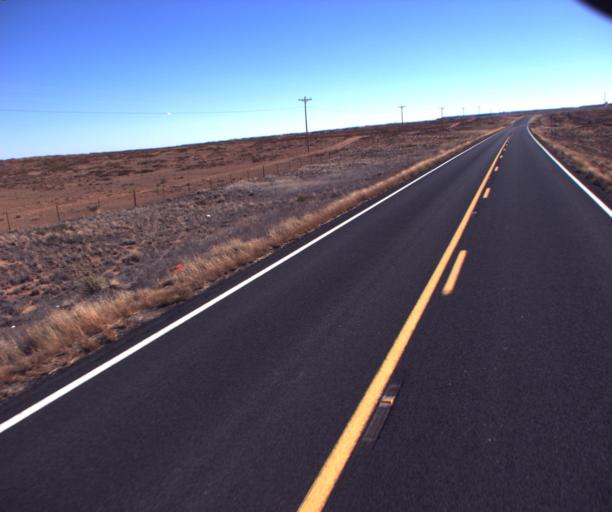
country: US
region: Arizona
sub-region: Coconino County
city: Tuba City
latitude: 36.0073
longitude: -111.0551
